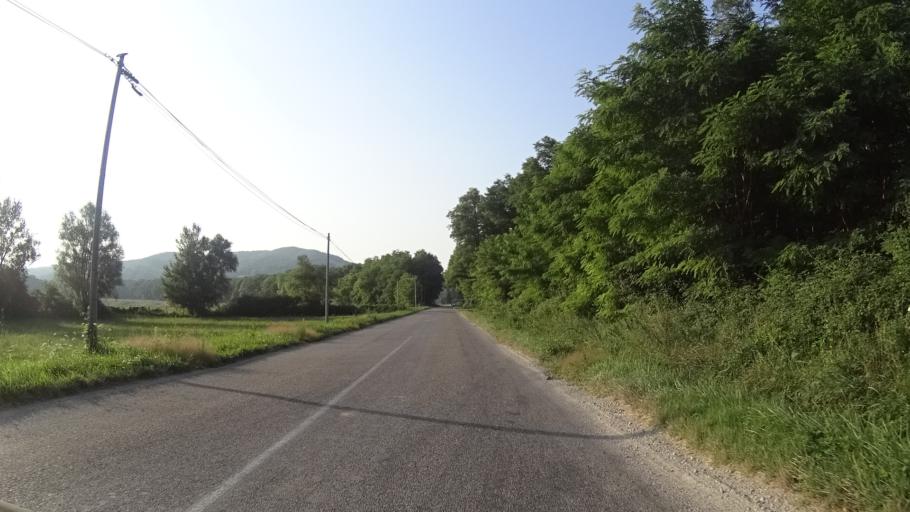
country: FR
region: Midi-Pyrenees
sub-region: Departement de l'Ariege
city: Mirepoix
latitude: 43.0789
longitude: 1.9361
